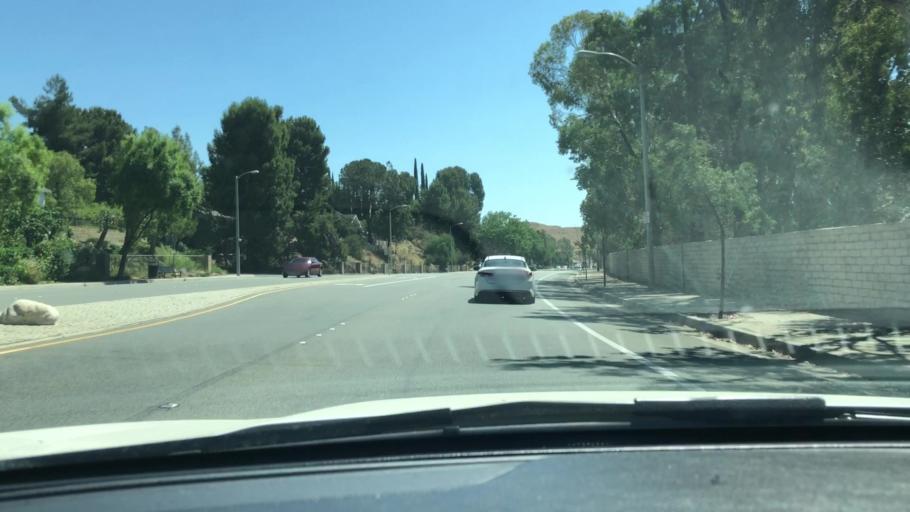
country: US
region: California
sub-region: Los Angeles County
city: Santa Clarita
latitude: 34.4260
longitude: -118.4298
